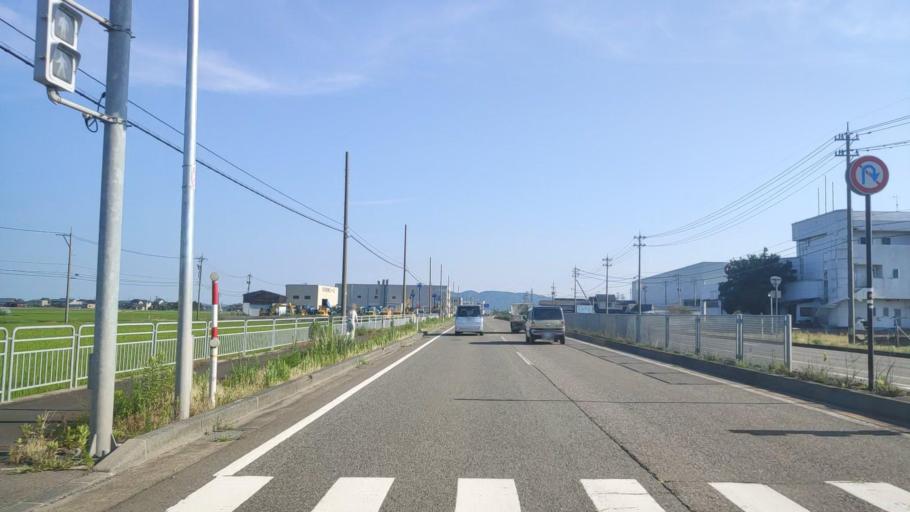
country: JP
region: Fukui
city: Maruoka
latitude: 36.1640
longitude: 136.2636
